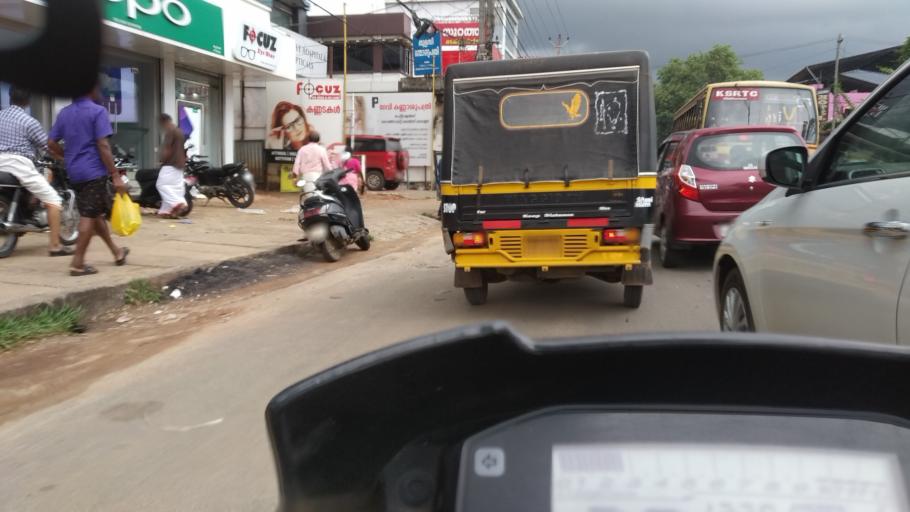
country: IN
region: Kerala
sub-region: Thiruvananthapuram
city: Attingal
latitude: 8.6989
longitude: 76.8136
